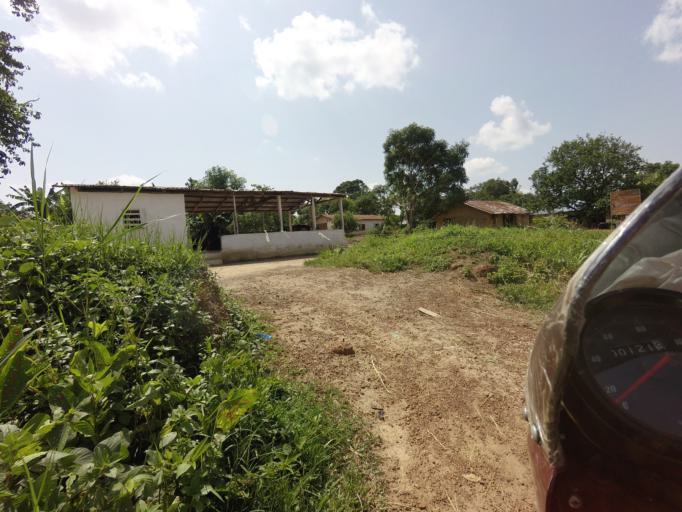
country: SL
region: Eastern Province
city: Manowa
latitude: 8.1720
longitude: -10.7513
